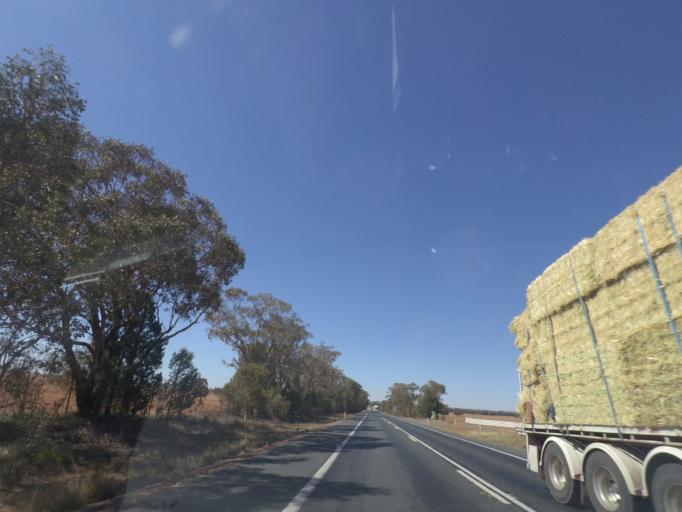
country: AU
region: New South Wales
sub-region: Bland
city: West Wyalong
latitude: -34.1820
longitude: 147.1132
